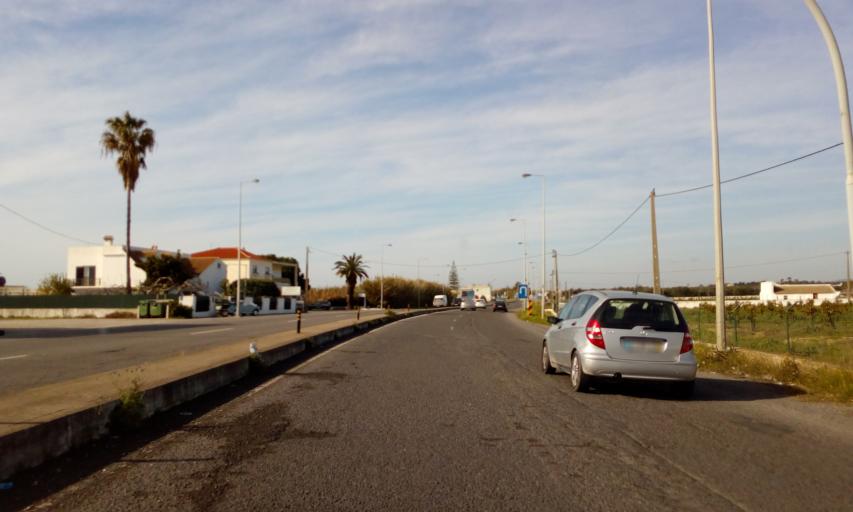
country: PT
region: Faro
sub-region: Olhao
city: Olhao
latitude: 37.0296
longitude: -7.8606
